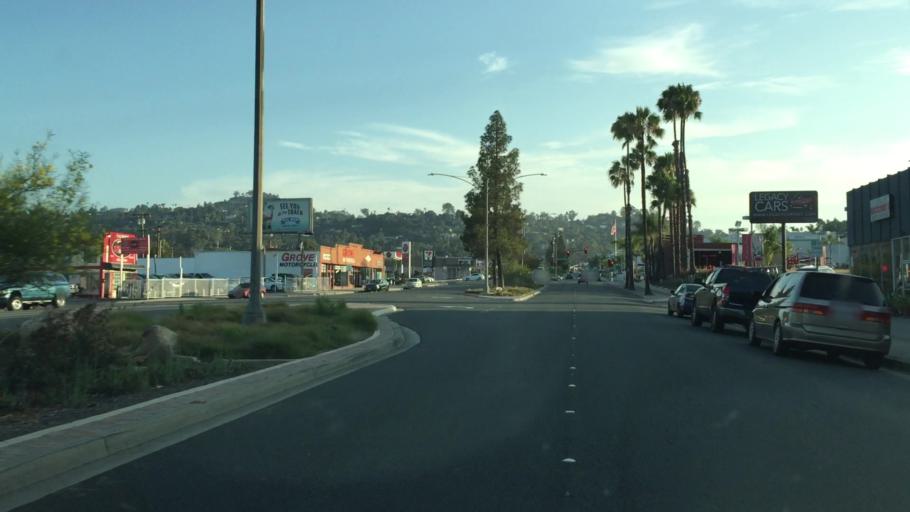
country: US
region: California
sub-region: San Diego County
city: El Cajon
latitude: 32.7891
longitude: -116.9736
